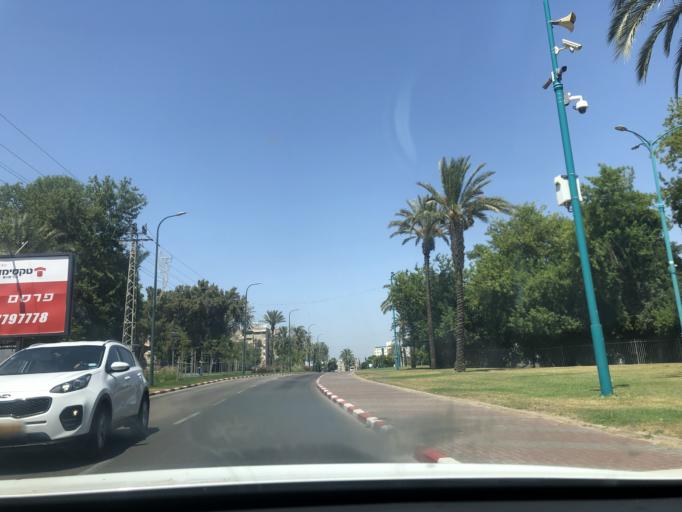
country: IL
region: Central District
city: Lod
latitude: 31.9415
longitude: 34.8880
